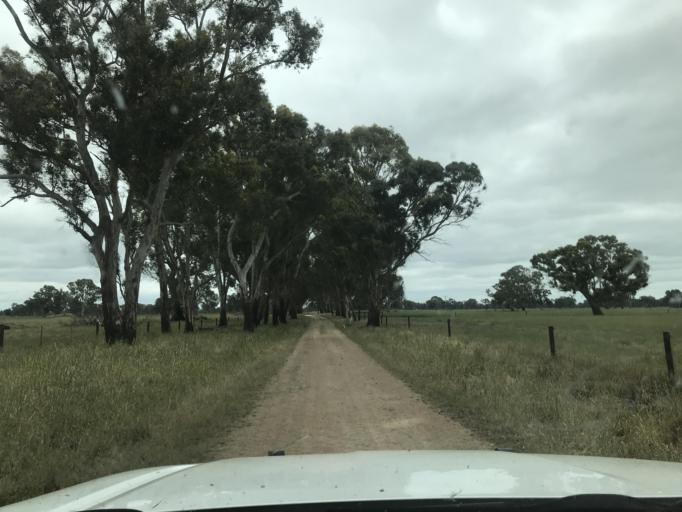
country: AU
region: South Australia
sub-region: Wattle Range
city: Penola
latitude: -37.1782
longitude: 141.0502
